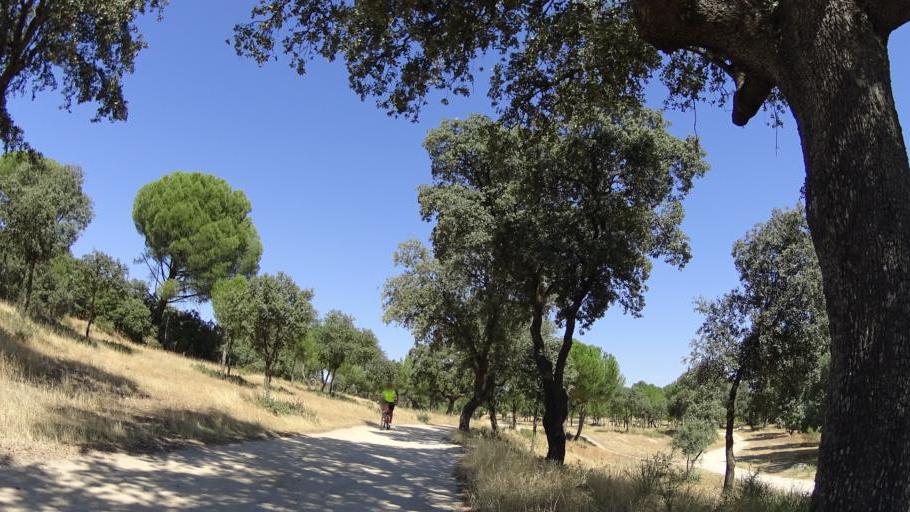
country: ES
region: Madrid
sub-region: Provincia de Madrid
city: Boadilla del Monte
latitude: 40.4249
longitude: -3.8538
